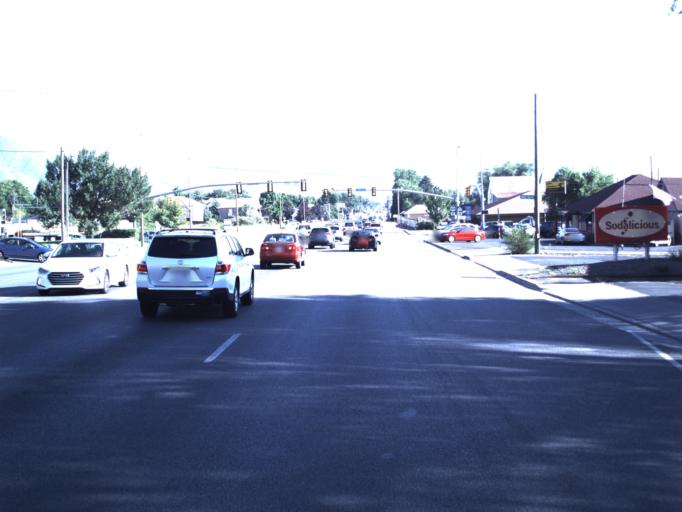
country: US
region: Utah
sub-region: Utah County
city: Springville
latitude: 40.1867
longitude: -111.6108
